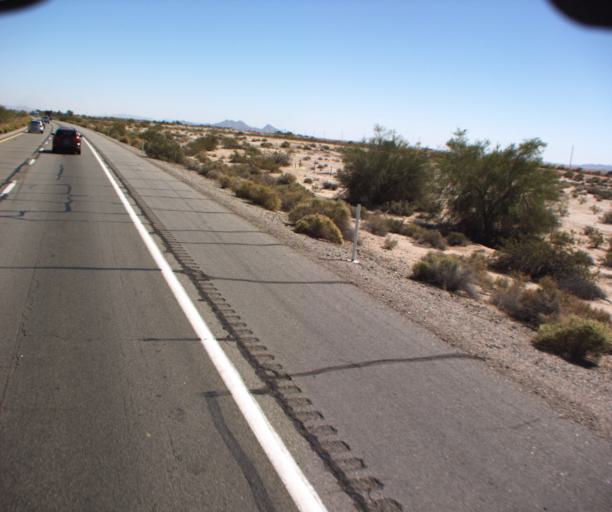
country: US
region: Arizona
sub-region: Yuma County
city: Wellton
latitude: 32.6491
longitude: -114.1961
